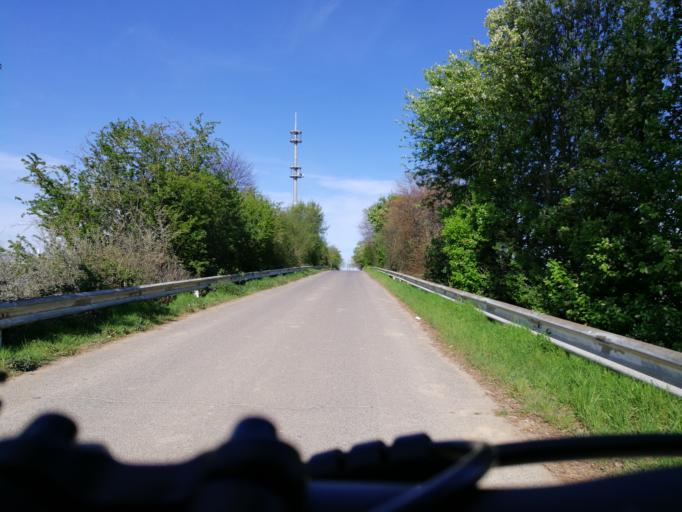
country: DE
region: North Rhine-Westphalia
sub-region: Regierungsbezirk Dusseldorf
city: Dormagen
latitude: 51.1424
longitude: 6.7674
